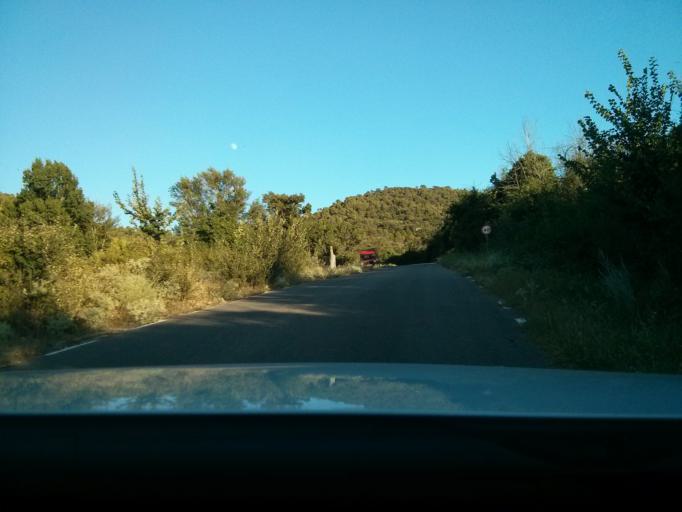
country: ES
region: Castille-La Mancha
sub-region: Provincia de Guadalajara
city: Mantiel
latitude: 40.6214
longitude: -2.6387
